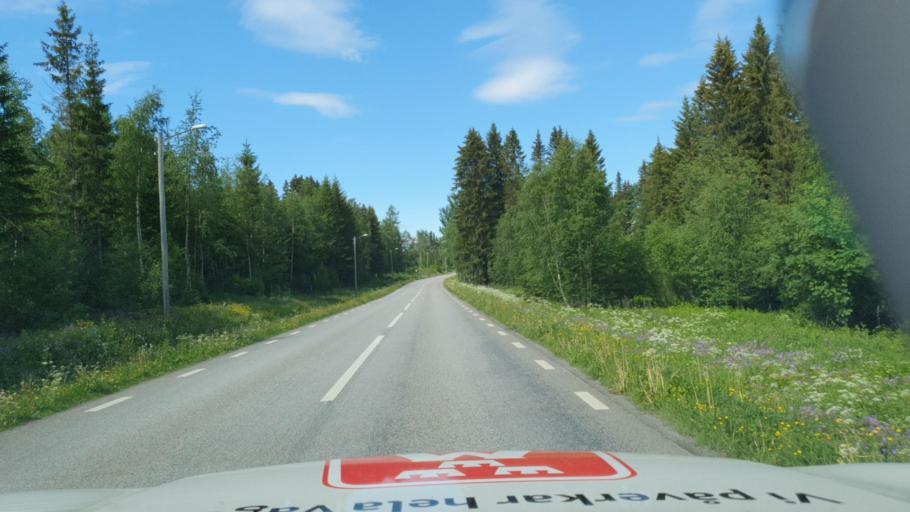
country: SE
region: Jaemtland
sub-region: Krokoms Kommun
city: Krokom
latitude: 63.1512
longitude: 14.1595
